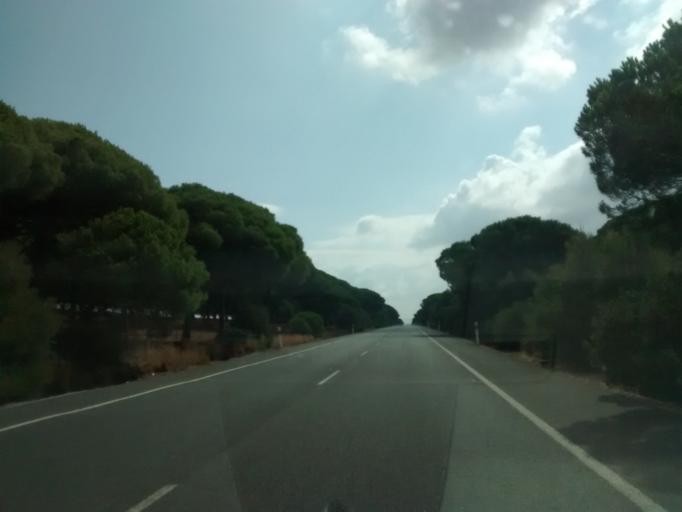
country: ES
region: Andalusia
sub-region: Provincia de Cadiz
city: Barbate de Franco
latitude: 36.2474
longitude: -5.9120
